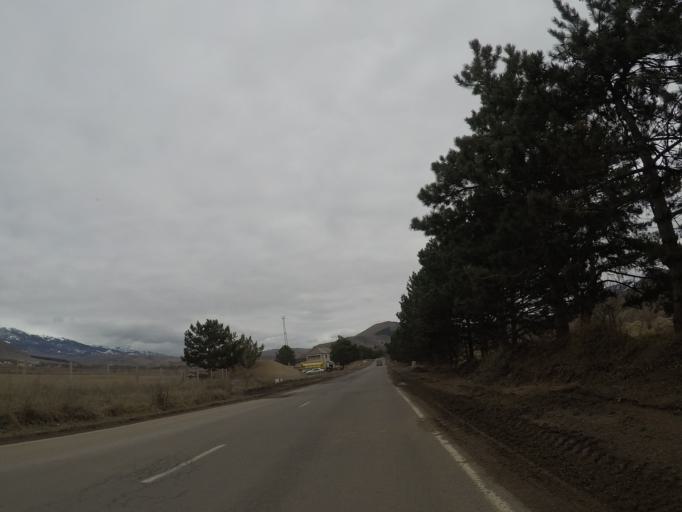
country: GE
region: Samtskhe-Javakheti
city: Aspindza
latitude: 41.6151
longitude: 43.1204
